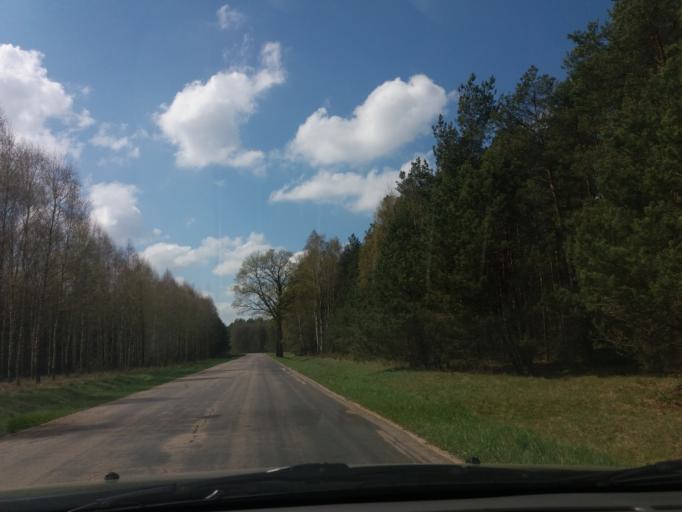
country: PL
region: Warmian-Masurian Voivodeship
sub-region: Powiat szczycienski
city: Jedwabno
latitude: 53.3605
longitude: 20.6879
